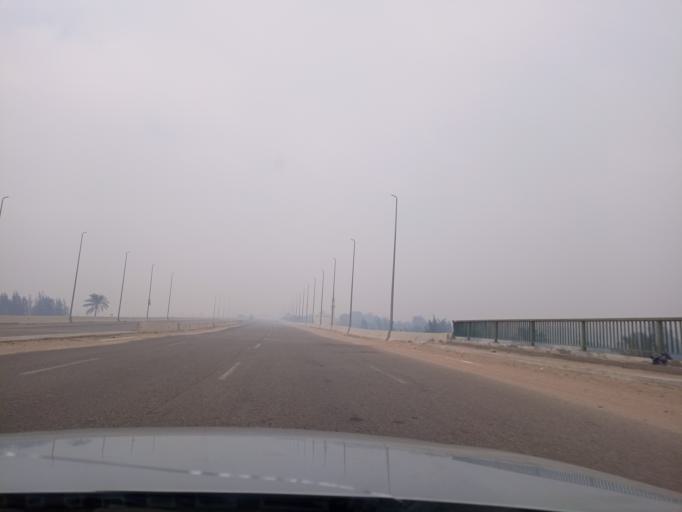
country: EG
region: Al Jizah
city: Al `Ayyat
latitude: 29.6839
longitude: 31.2334
